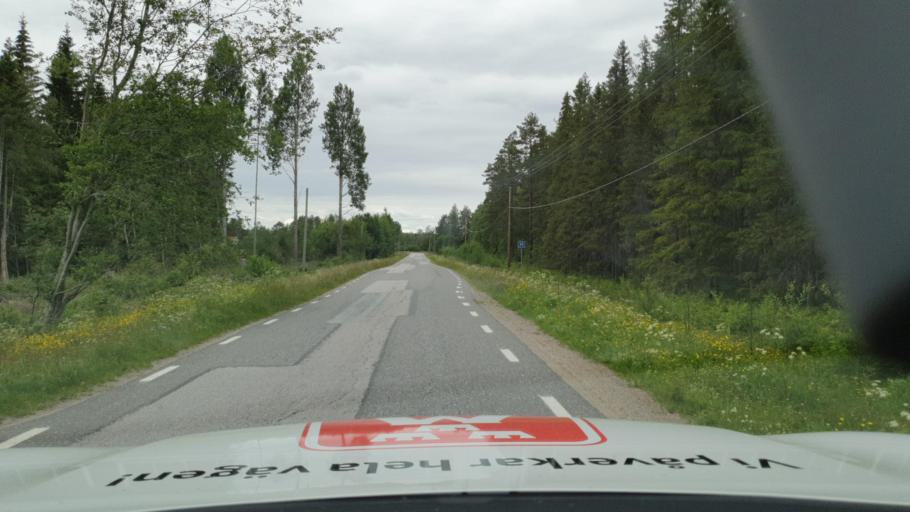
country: SE
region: Vaesterbotten
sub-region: Nordmalings Kommun
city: Nordmaling
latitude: 63.5234
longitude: 19.4166
